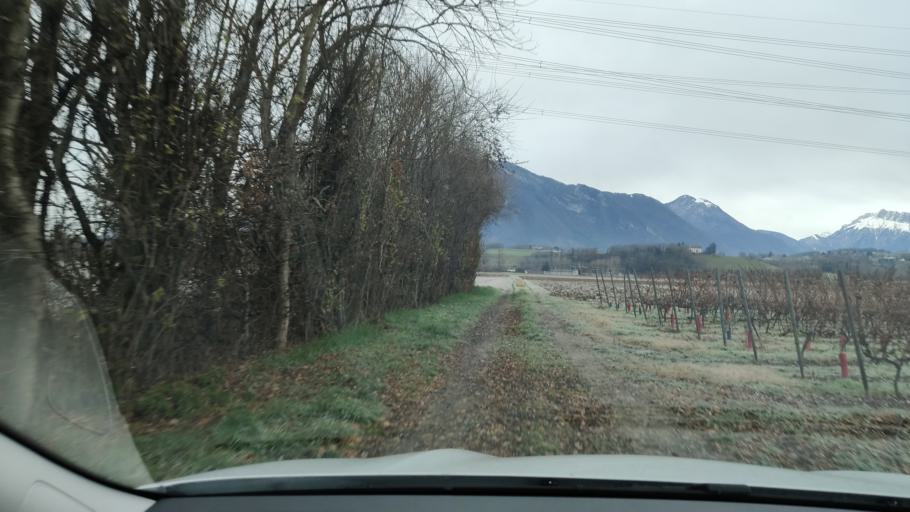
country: FR
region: Rhone-Alpes
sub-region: Departement de la Savoie
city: Montmelian
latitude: 45.4654
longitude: 6.0406
